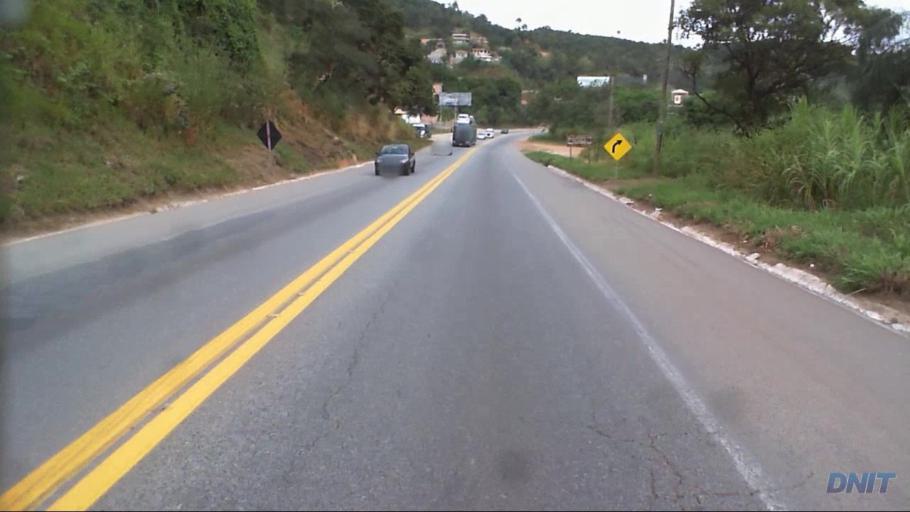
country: BR
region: Minas Gerais
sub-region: Santa Luzia
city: Santa Luzia
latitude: -19.8376
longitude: -43.8612
